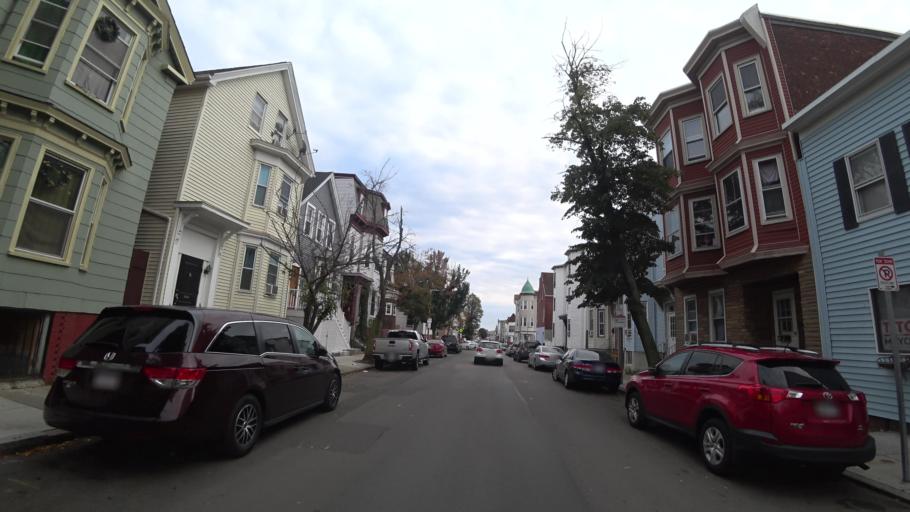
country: US
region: Massachusetts
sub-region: Suffolk County
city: Chelsea
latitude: 42.3803
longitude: -71.0387
